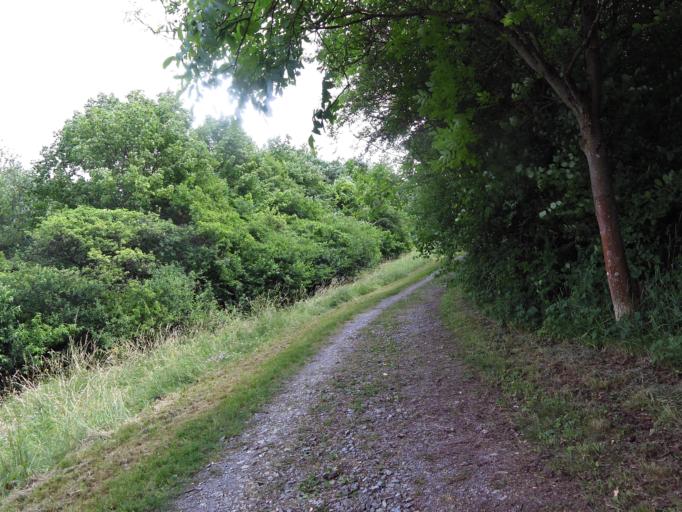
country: DE
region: Bavaria
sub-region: Regierungsbezirk Unterfranken
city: Wuerzburg
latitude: 49.7942
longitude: 9.9674
